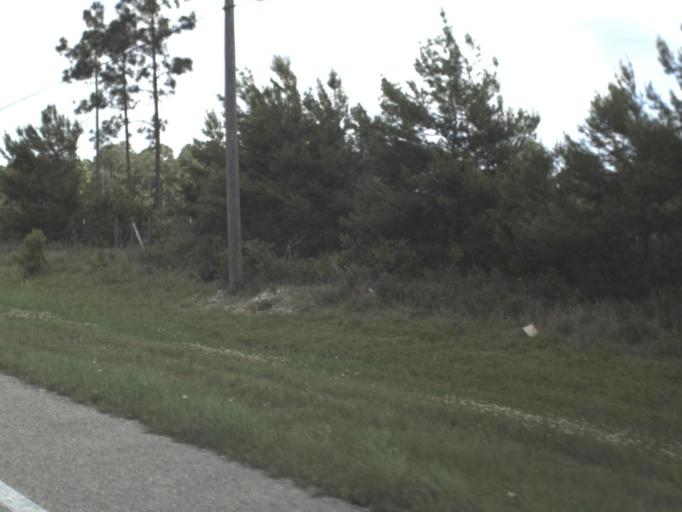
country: US
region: Florida
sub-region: Saint Johns County
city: Palm Valley
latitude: 30.0402
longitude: -81.4168
